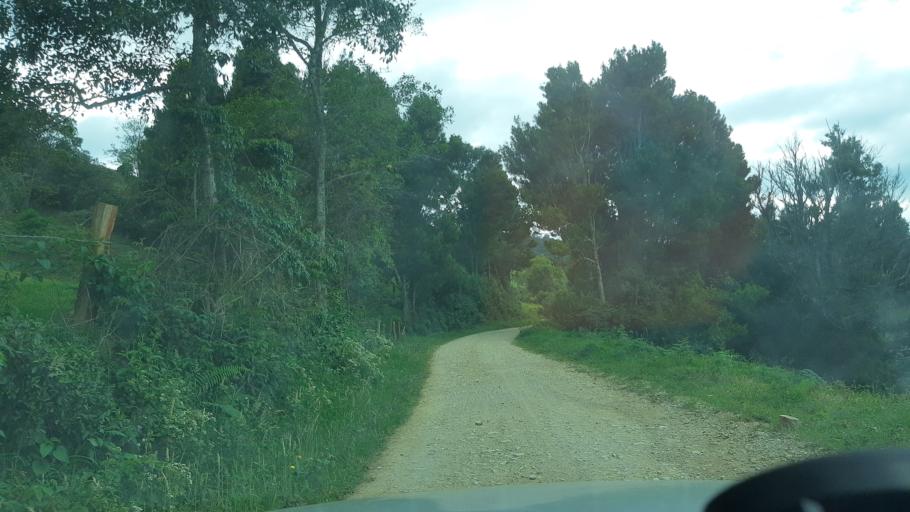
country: CO
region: Boyaca
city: Santa Sofia
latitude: 5.7479
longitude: -73.5507
